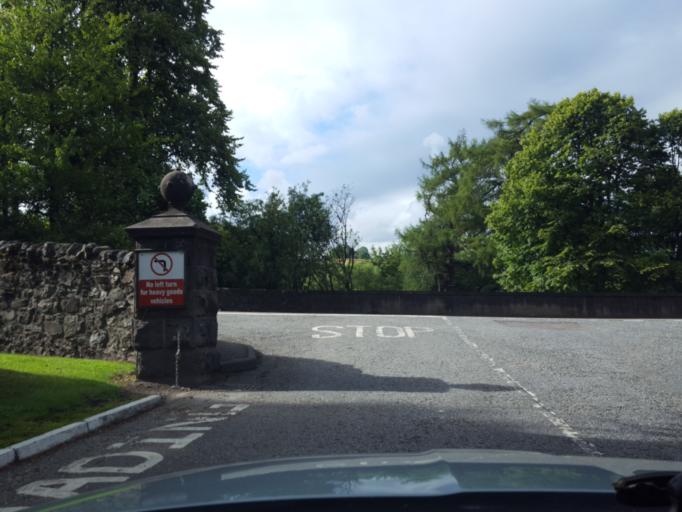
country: GB
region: Scotland
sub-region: Moray
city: Rothes
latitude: 57.4681
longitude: -3.2292
